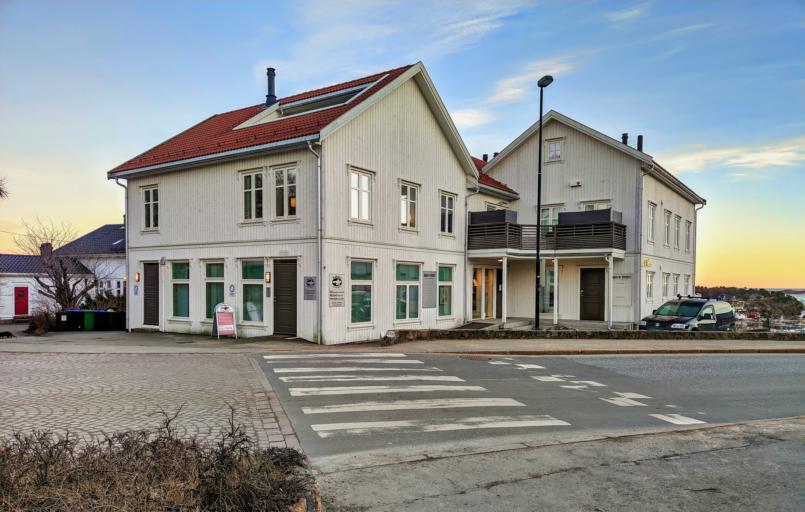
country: NO
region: Aust-Agder
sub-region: Grimstad
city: Fevik
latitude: 58.3807
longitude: 8.6762
